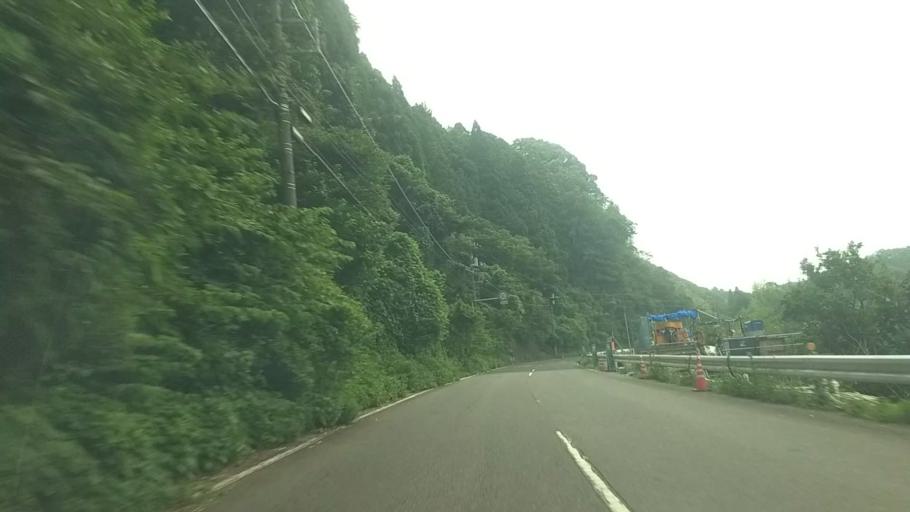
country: JP
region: Chiba
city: Katsuura
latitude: 35.2469
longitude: 140.2408
